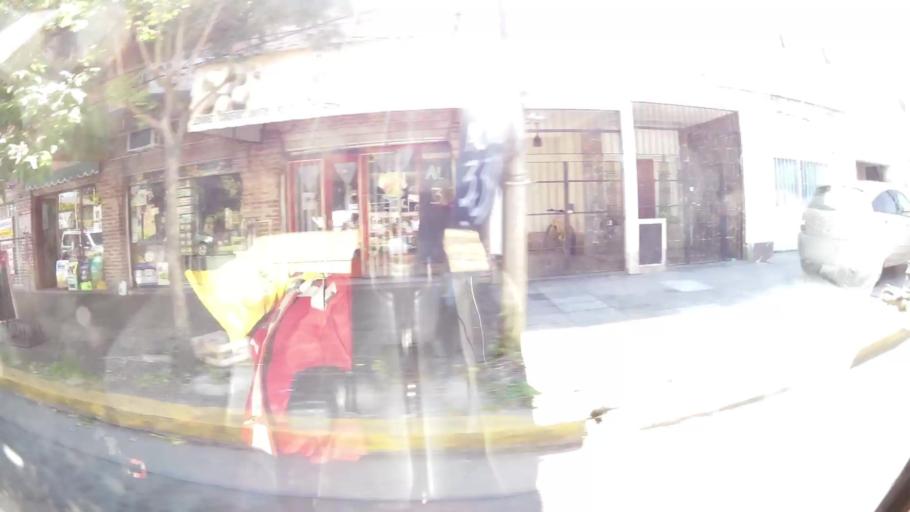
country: AR
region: Buenos Aires
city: Ituzaingo
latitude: -34.6604
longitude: -58.6637
